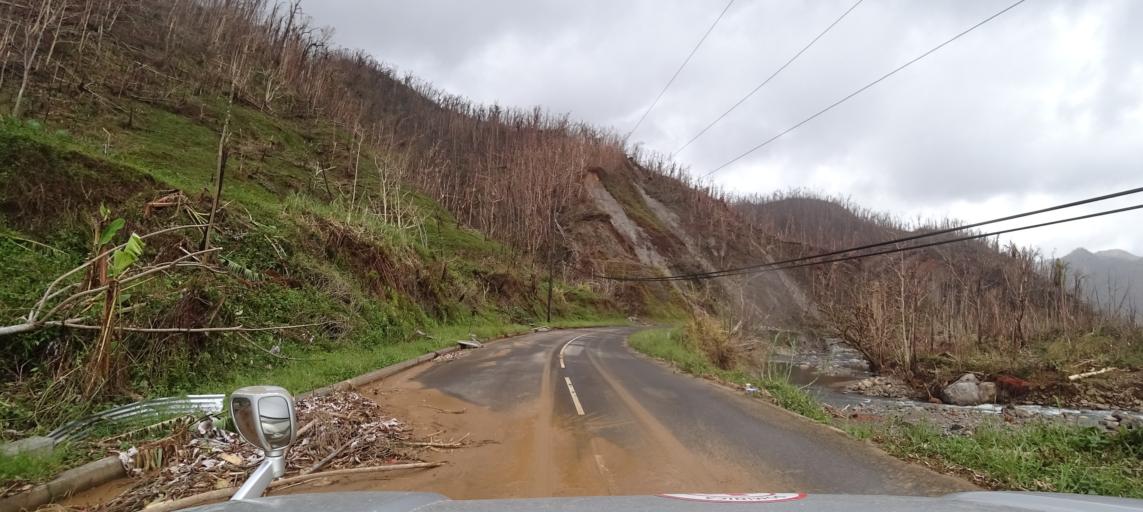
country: DM
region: Saint David
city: Castle Bruce
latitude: 15.4316
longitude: -61.3327
